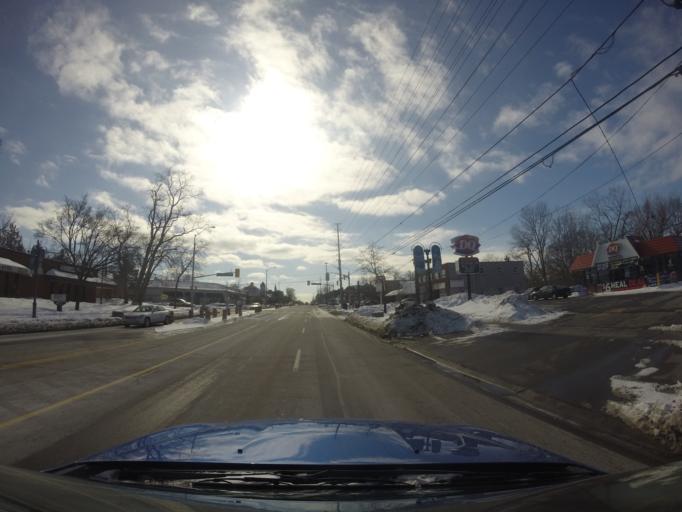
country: CA
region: Ontario
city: Mississauga
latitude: 43.5197
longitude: -79.6206
